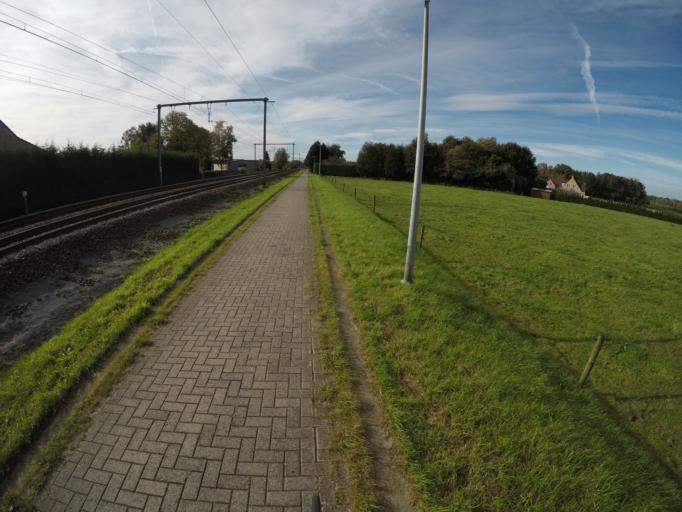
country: BE
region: Flanders
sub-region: Provincie Oost-Vlaanderen
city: Waasmunster
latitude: 51.1486
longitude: 4.0822
